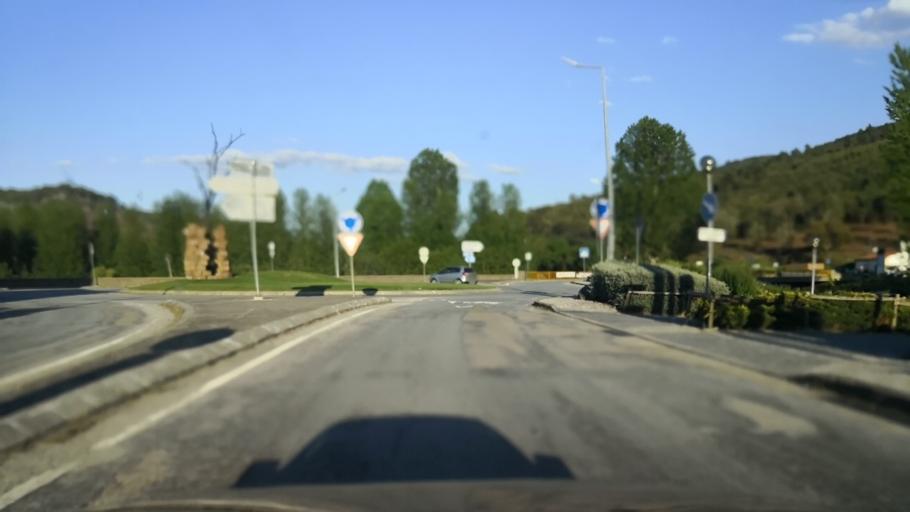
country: PT
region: Portalegre
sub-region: Marvao
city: Marvao
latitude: 39.3827
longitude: -7.3840
